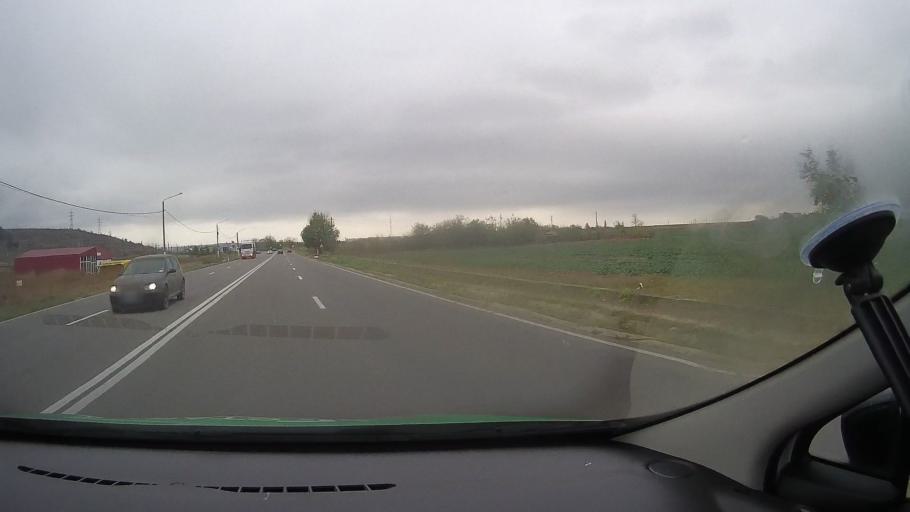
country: RO
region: Constanta
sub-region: Oras Murfatlar
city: Murfatlar
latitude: 44.1705
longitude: 28.4331
